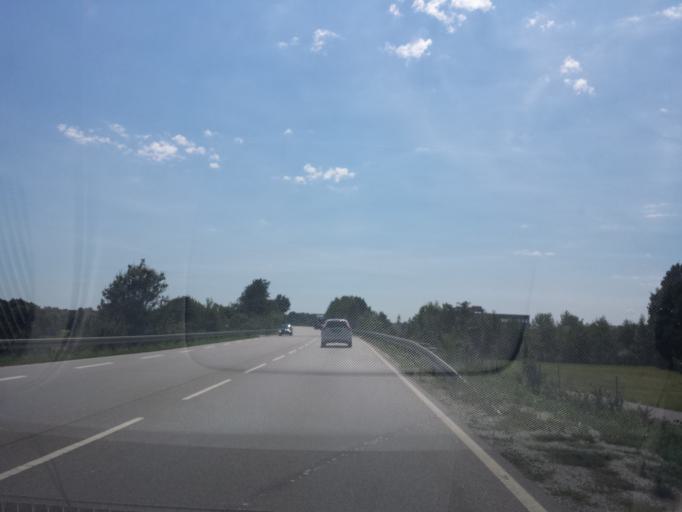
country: DE
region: Bavaria
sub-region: Lower Bavaria
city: Steinach
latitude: 48.9477
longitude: 12.6201
